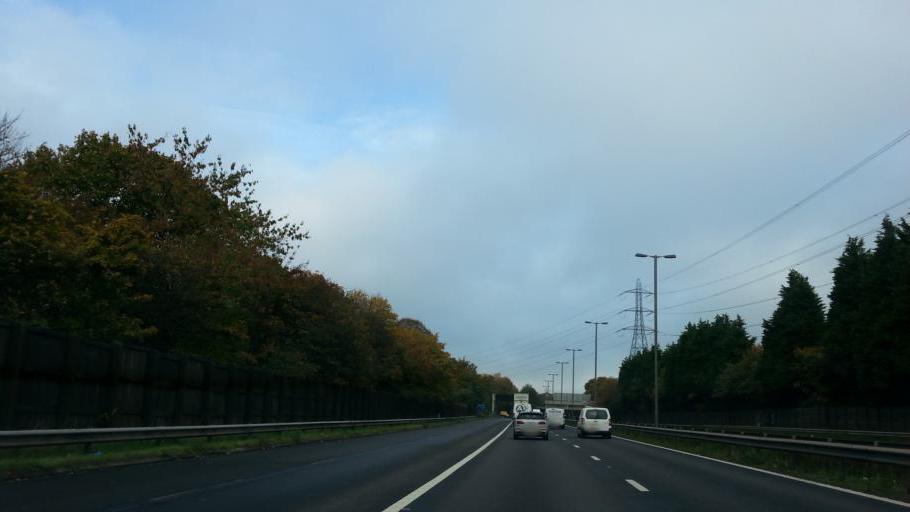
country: GB
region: England
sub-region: City and Borough of Birmingham
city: Bartley Green
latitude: 52.4575
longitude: -2.0124
